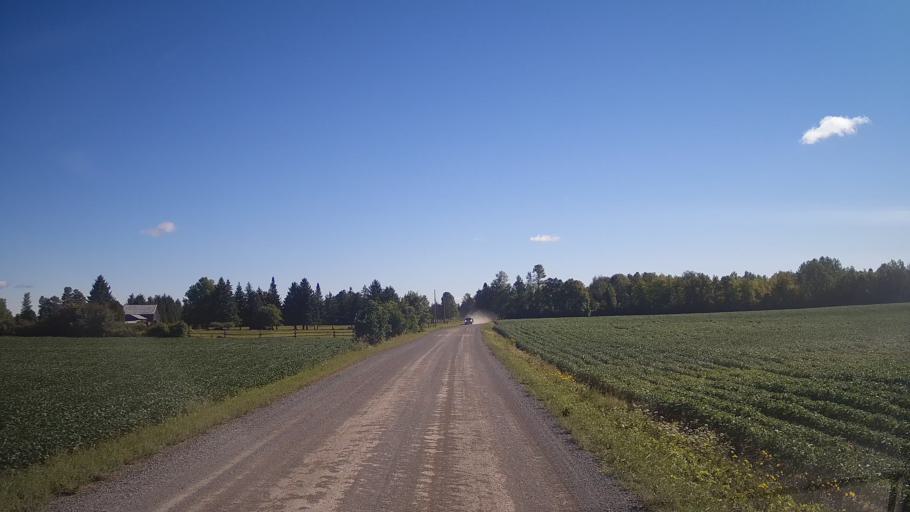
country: CA
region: Ontario
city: Prescott
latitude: 44.9735
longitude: -75.5574
